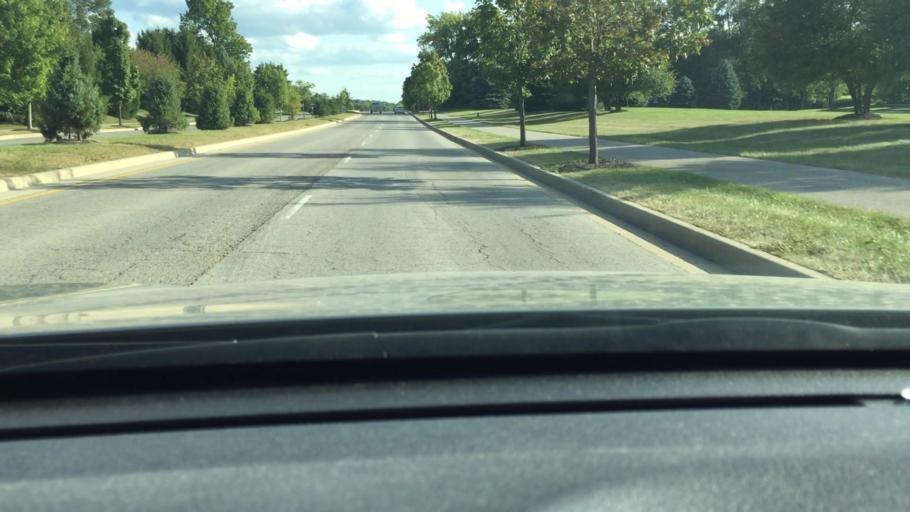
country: US
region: Indiana
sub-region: Hamilton County
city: Carmel
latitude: 39.9838
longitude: -86.0706
